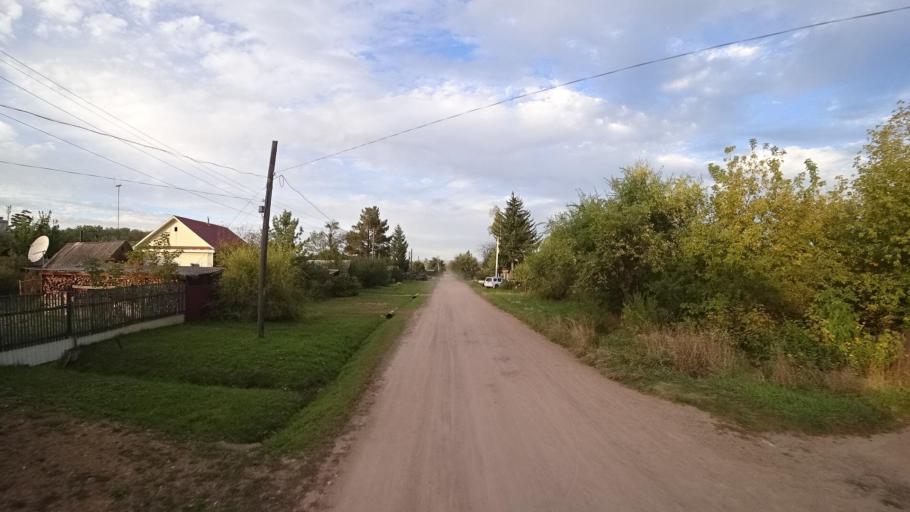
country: RU
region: Primorskiy
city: Yakovlevka
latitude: 44.4218
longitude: 133.4775
